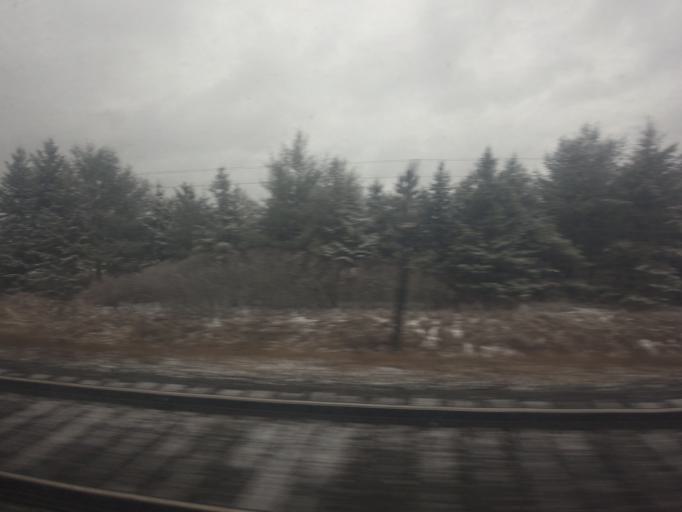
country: CA
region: Ontario
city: Gananoque
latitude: 44.3858
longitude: -76.0586
